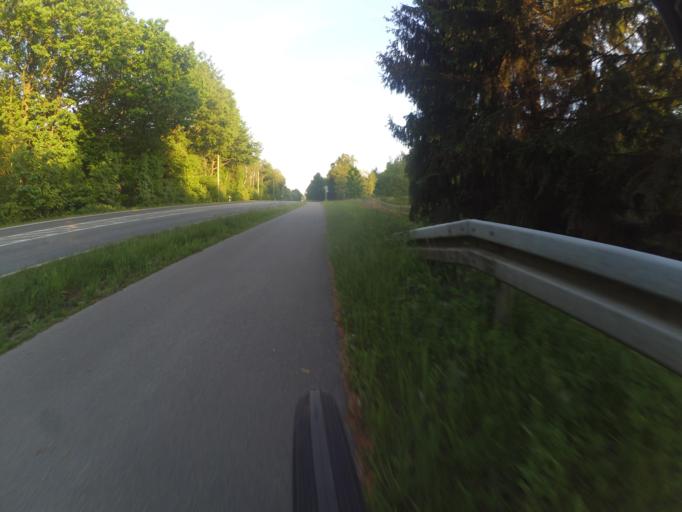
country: DE
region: North Rhine-Westphalia
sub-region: Regierungsbezirk Munster
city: Hopsten
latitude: 52.3326
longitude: 7.6644
